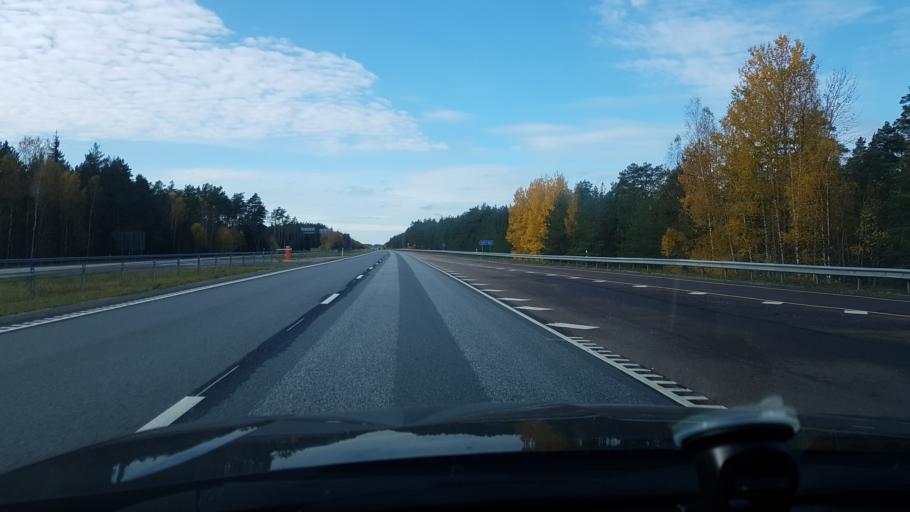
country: EE
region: Harju
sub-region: Kuusalu vald
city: Kuusalu
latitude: 59.4559
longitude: 25.5131
